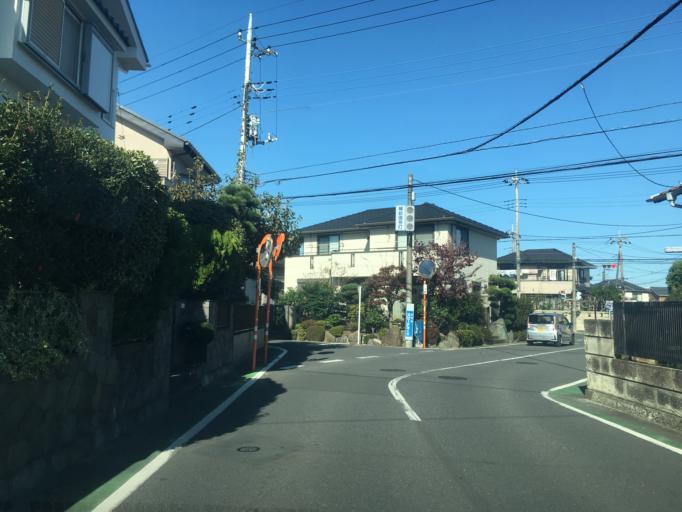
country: JP
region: Saitama
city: Sakado
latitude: 35.9632
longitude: 139.4080
